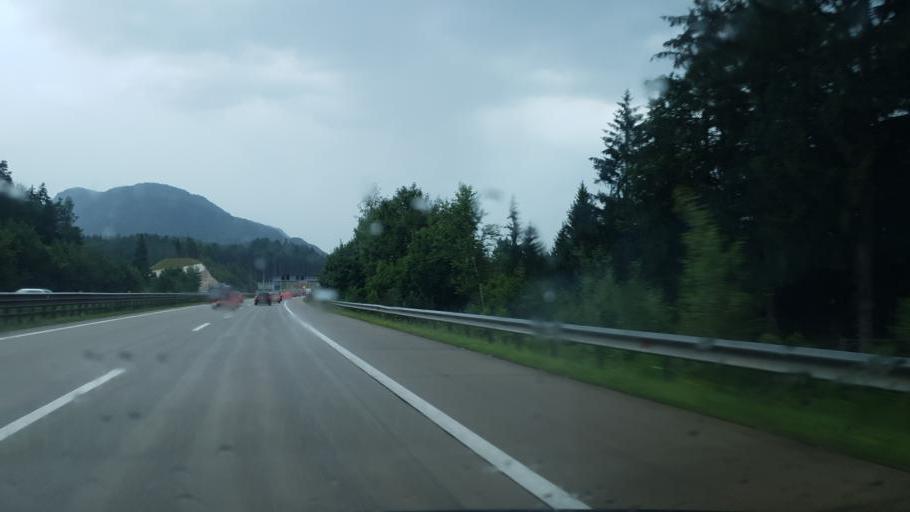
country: AT
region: Carinthia
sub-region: Politischer Bezirk Villach Land
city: Fresach
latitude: 46.6516
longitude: 13.7464
